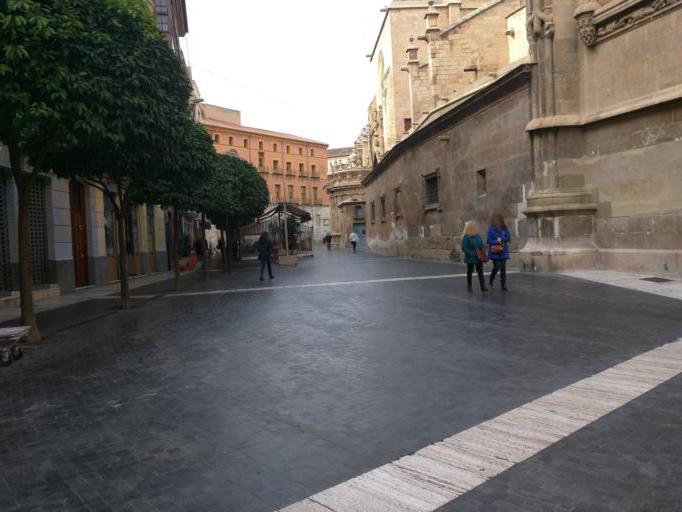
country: ES
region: Murcia
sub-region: Murcia
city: Murcia
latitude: 37.9839
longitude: -1.1280
